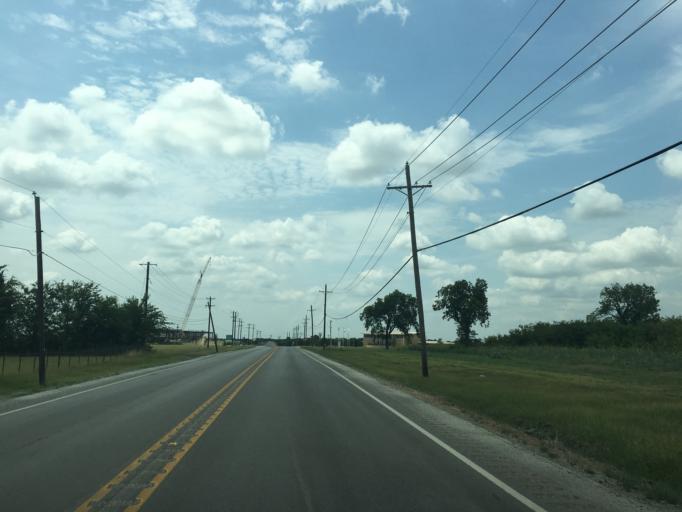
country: US
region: Texas
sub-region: Rockwall County
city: Fate
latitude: 32.9579
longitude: -96.3787
